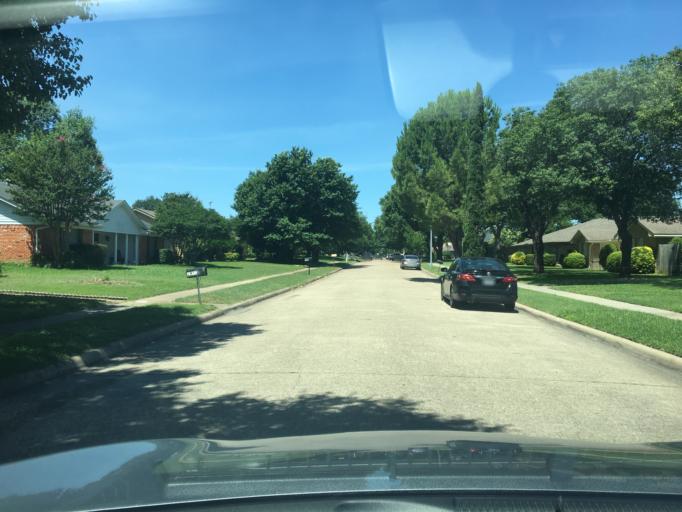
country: US
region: Texas
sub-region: Dallas County
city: Richardson
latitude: 32.9475
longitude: -96.6875
